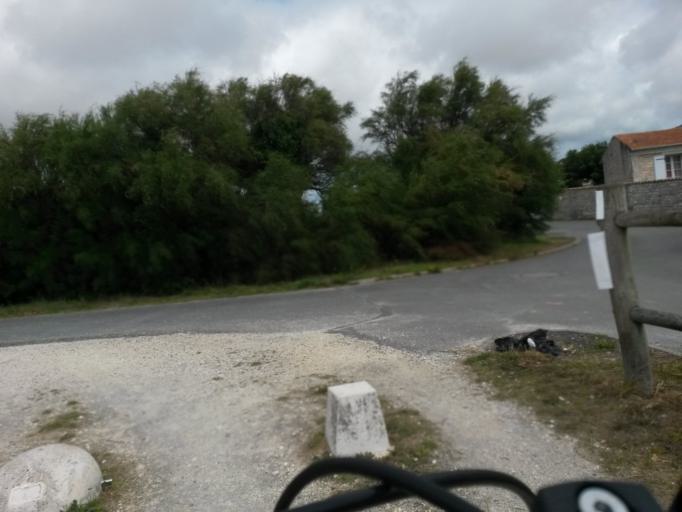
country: FR
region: Poitou-Charentes
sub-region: Departement de la Charente-Maritime
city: Dolus-d'Oleron
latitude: 45.9379
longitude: -1.2764
